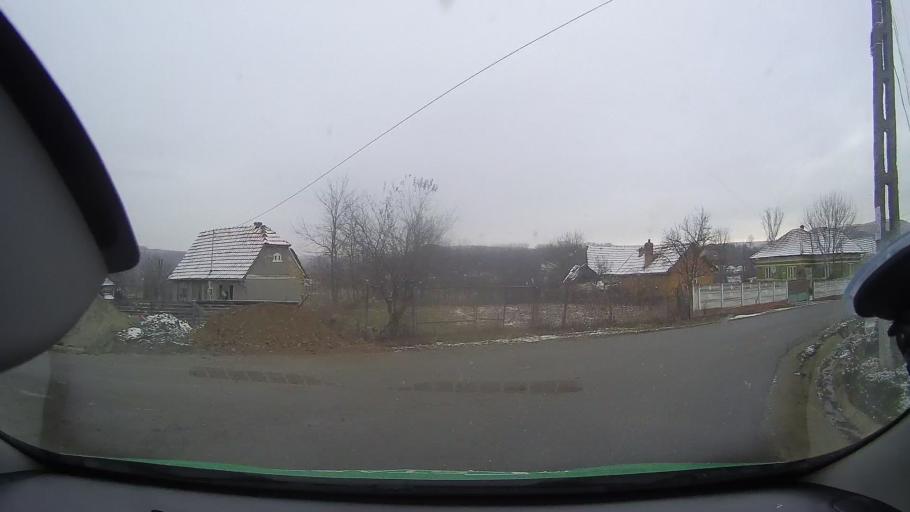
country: RO
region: Alba
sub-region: Comuna Farau
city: Farau
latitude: 46.3383
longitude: 24.0039
